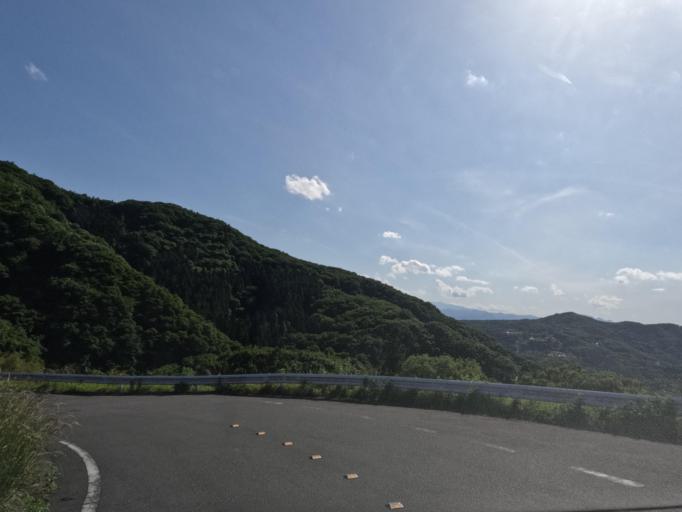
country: JP
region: Saitama
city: Yorii
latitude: 36.0500
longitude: 139.1467
